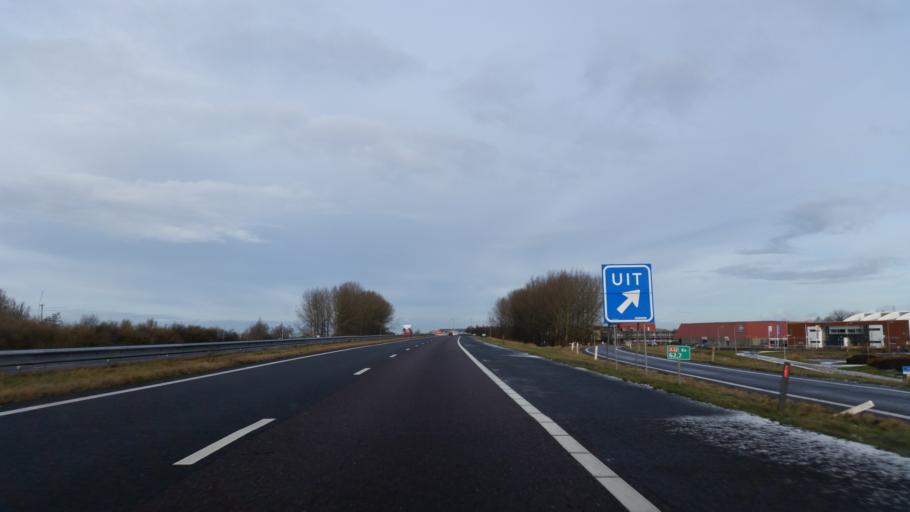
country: NL
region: Friesland
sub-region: Gemeente Boarnsterhim
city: Grou
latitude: 53.0875
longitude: 5.8248
